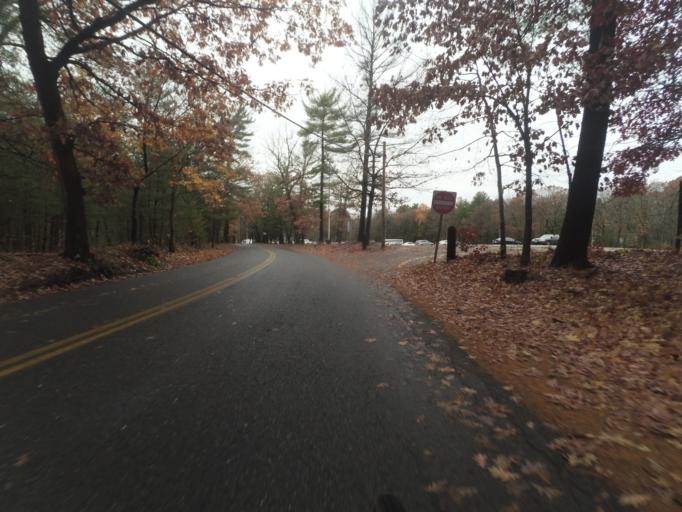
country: US
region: Massachusetts
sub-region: Middlesex County
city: Bedford
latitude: 42.5106
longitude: -71.2740
